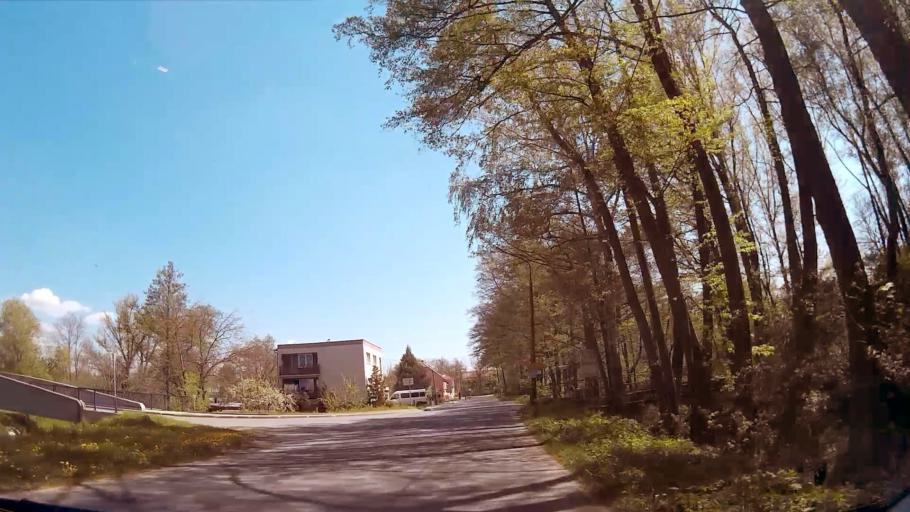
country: CZ
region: South Moravian
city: Ivancice
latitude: 49.0935
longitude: 16.3616
